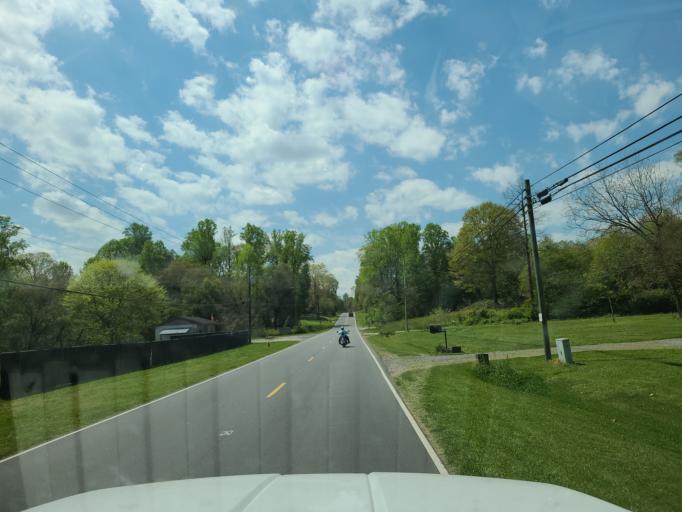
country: US
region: North Carolina
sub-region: Lincoln County
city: Lincolnton
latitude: 35.4549
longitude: -81.2750
